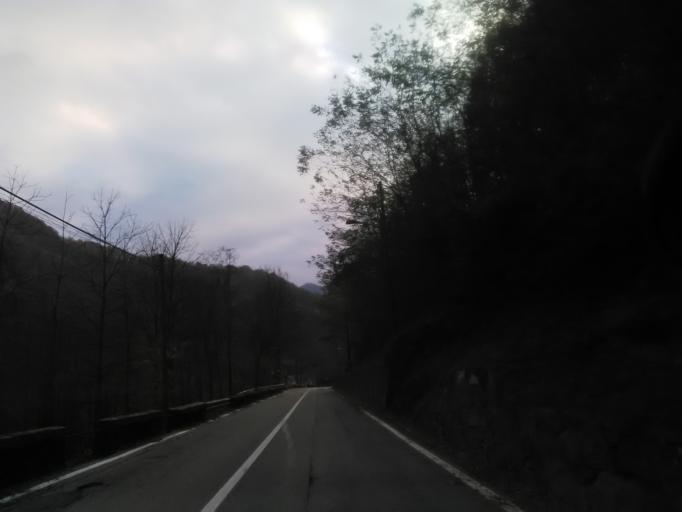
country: IT
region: Piedmont
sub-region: Provincia di Vercelli
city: Varallo
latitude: 45.8308
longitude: 8.2550
